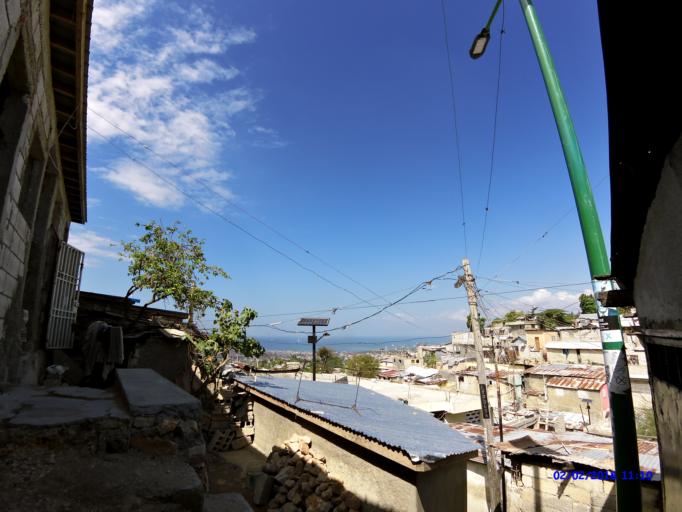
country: HT
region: Ouest
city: Port-au-Prince
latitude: 18.5248
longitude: -72.3334
